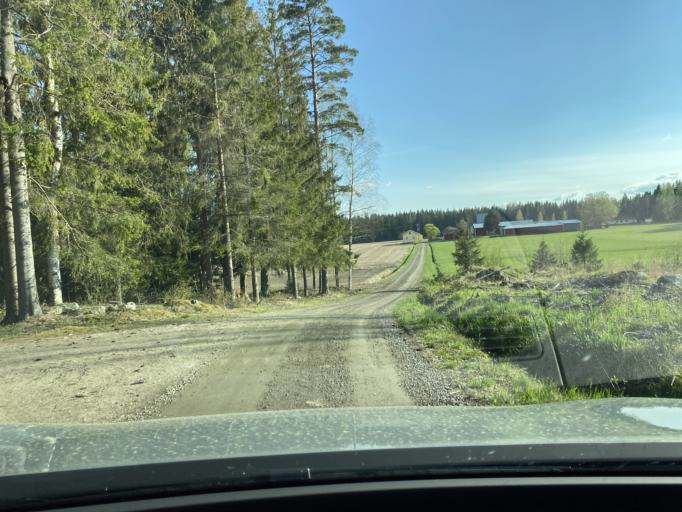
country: FI
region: Pirkanmaa
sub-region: Lounais-Pirkanmaa
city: Punkalaidun
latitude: 61.0236
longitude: 23.2158
